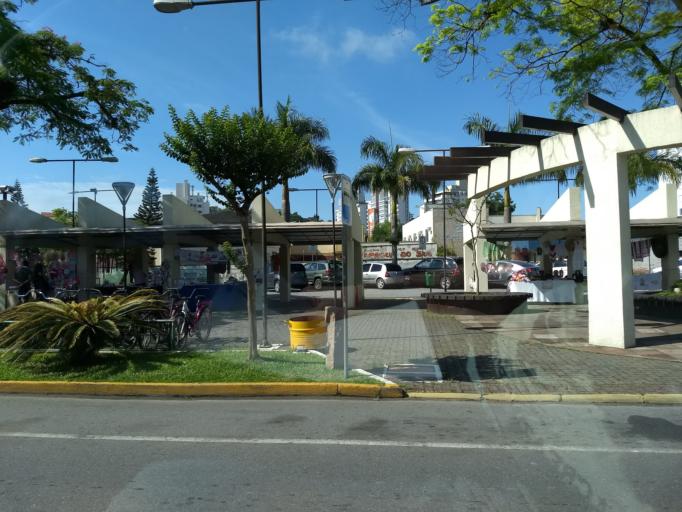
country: BR
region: Santa Catarina
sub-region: Jaragua Do Sul
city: Jaragua do Sul
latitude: -26.4794
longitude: -49.0865
